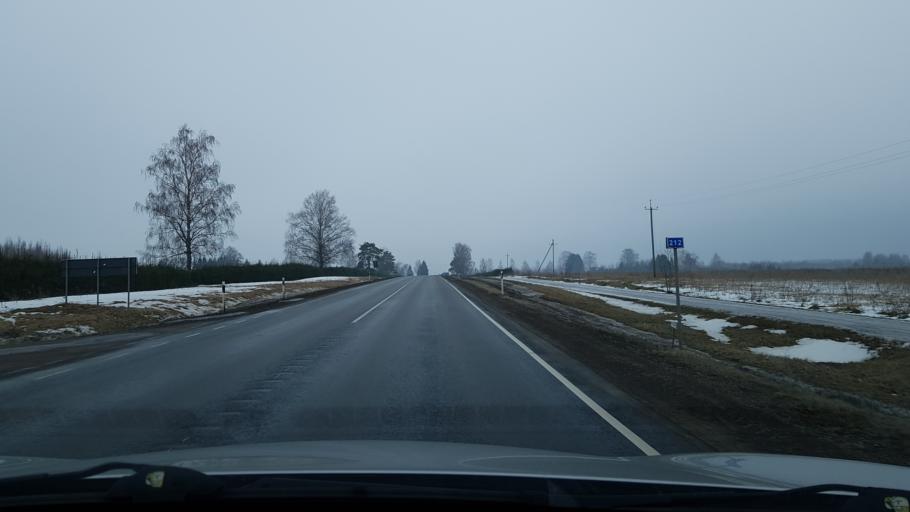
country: EE
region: Valgamaa
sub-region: Valga linn
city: Valga
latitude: 57.8278
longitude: 26.1126
